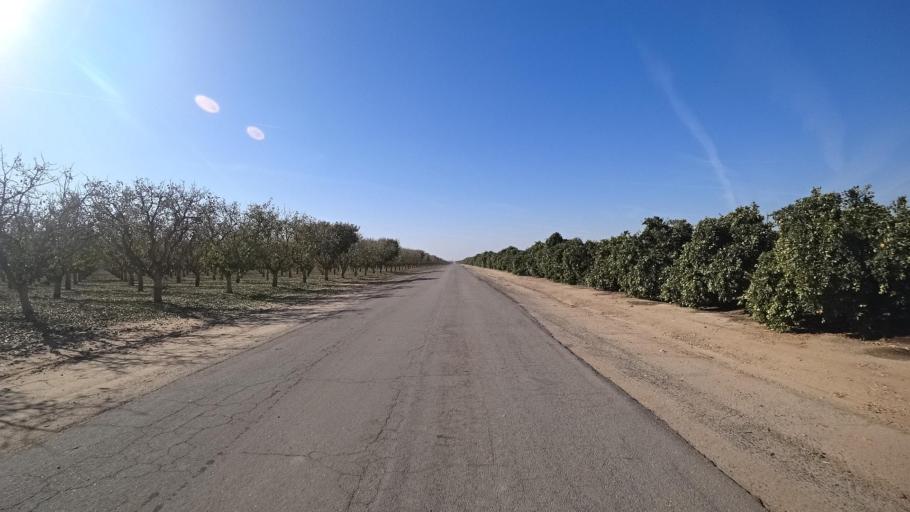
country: US
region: California
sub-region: Kern County
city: McFarland
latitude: 35.6454
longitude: -119.1698
